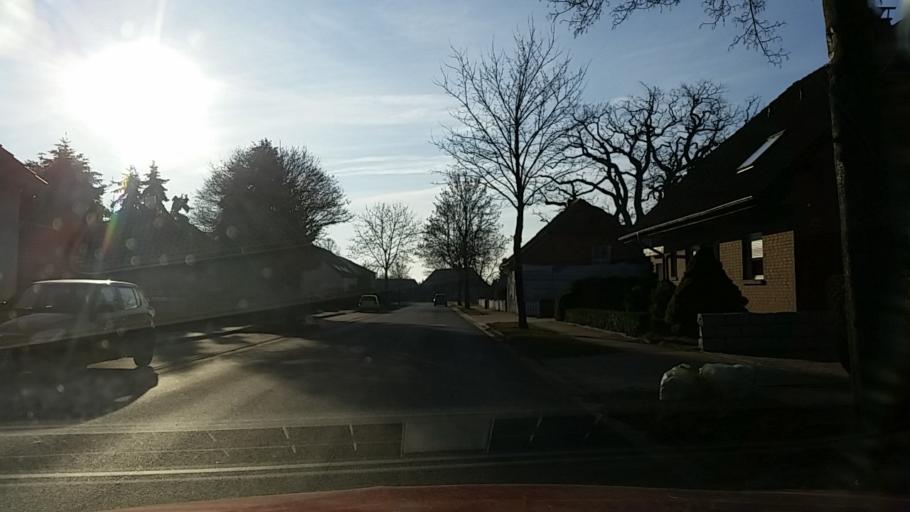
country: DE
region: Lower Saxony
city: Ruhen
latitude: 52.4858
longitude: 10.8443
